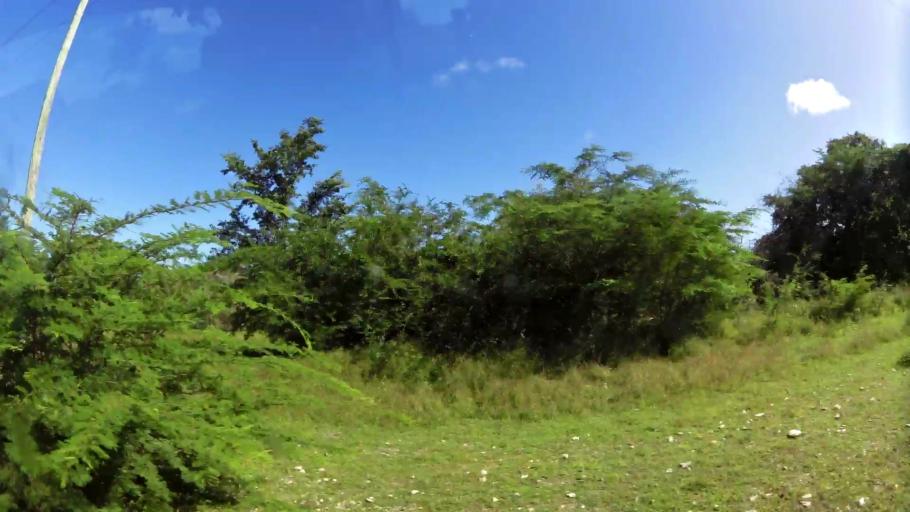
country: AG
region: Barbuda
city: Codrington
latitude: 17.6094
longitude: -61.8286
